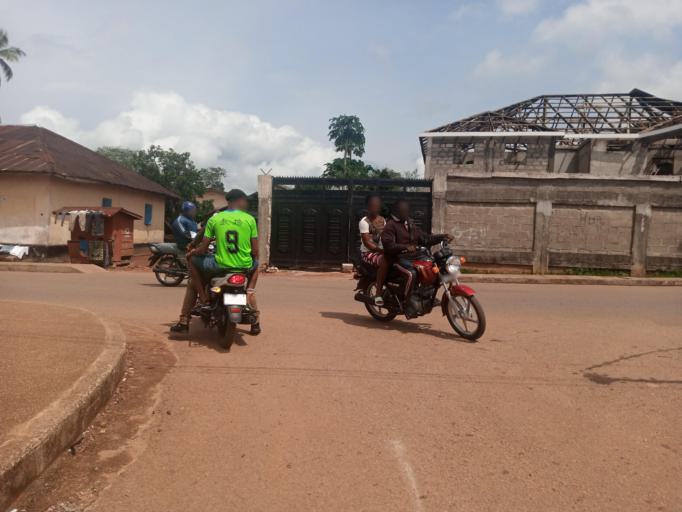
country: SL
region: Southern Province
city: Bo
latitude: 7.9697
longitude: -11.7403
